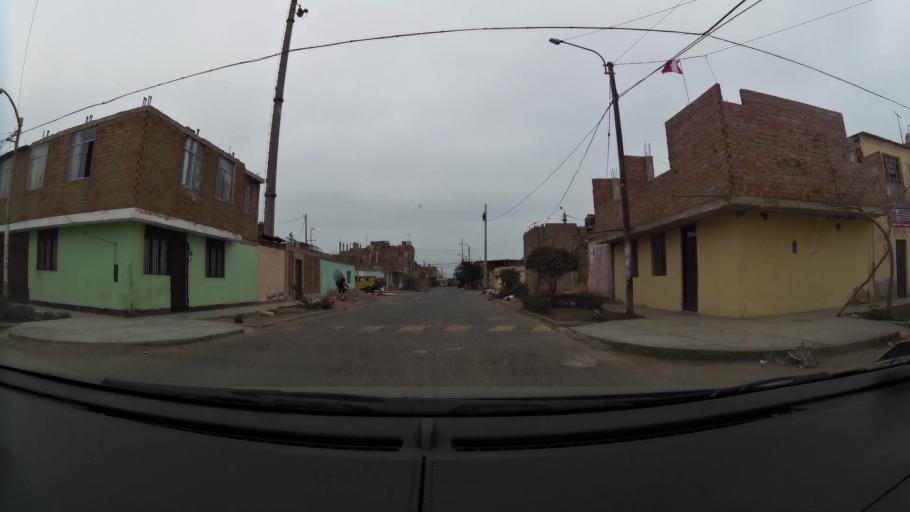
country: PE
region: La Libertad
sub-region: Provincia de Trujillo
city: Buenos Aires
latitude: -8.1407
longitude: -79.0578
